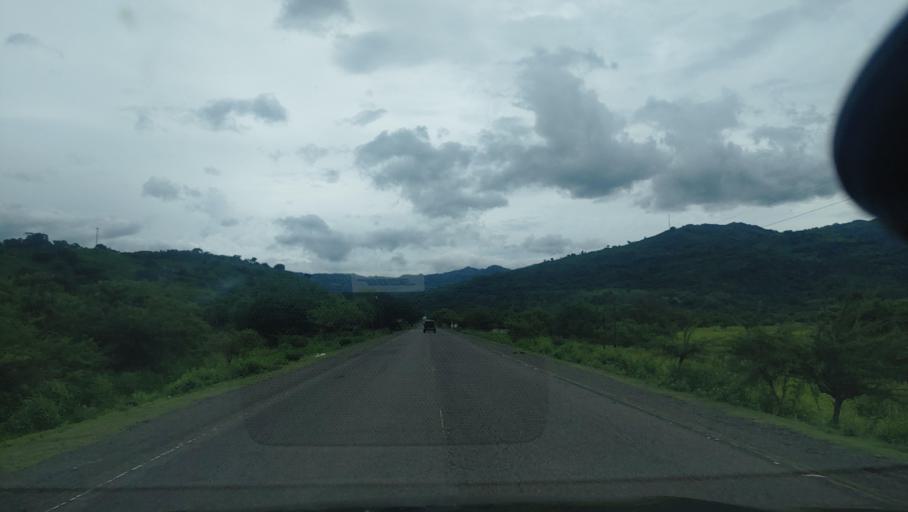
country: HN
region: Choluteca
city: Santa Ana de Yusguare
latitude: 13.3611
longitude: -87.0910
